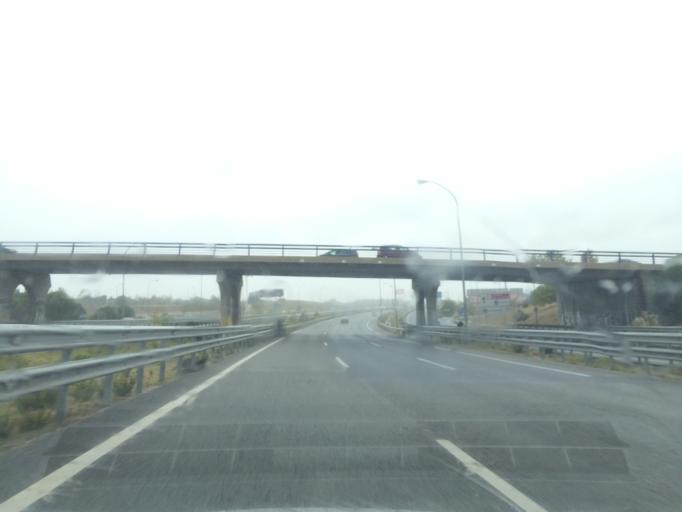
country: ES
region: Madrid
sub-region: Provincia de Madrid
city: Pozuelo de Alarcon
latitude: 40.4245
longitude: -3.8343
